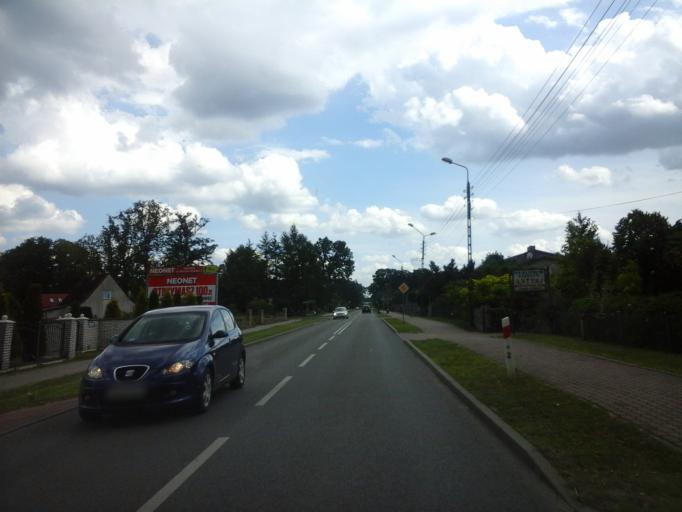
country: PL
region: West Pomeranian Voivodeship
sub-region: Powiat swidwinski
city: Slawoborze
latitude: 53.8897
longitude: 15.7139
